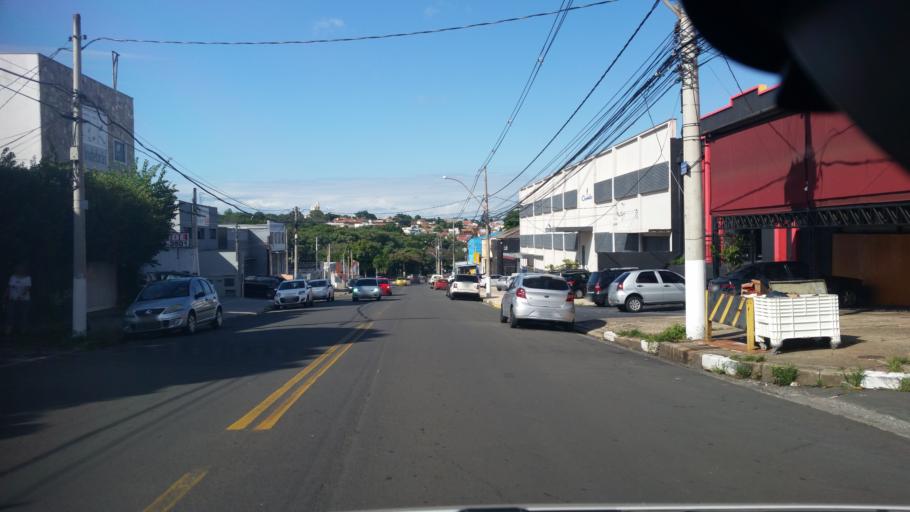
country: BR
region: Sao Paulo
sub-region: Campinas
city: Campinas
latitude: -22.8770
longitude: -47.0483
